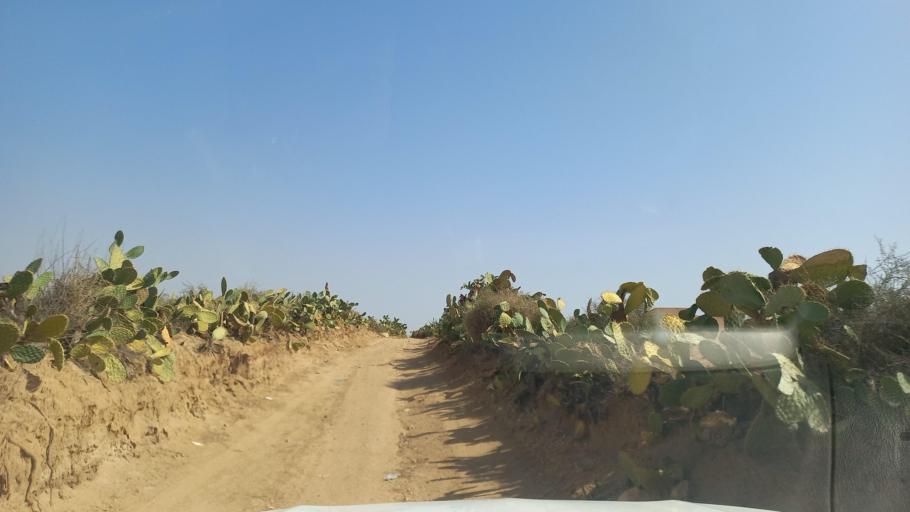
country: TN
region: Al Qasrayn
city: Kasserine
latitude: 35.2284
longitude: 9.0497
